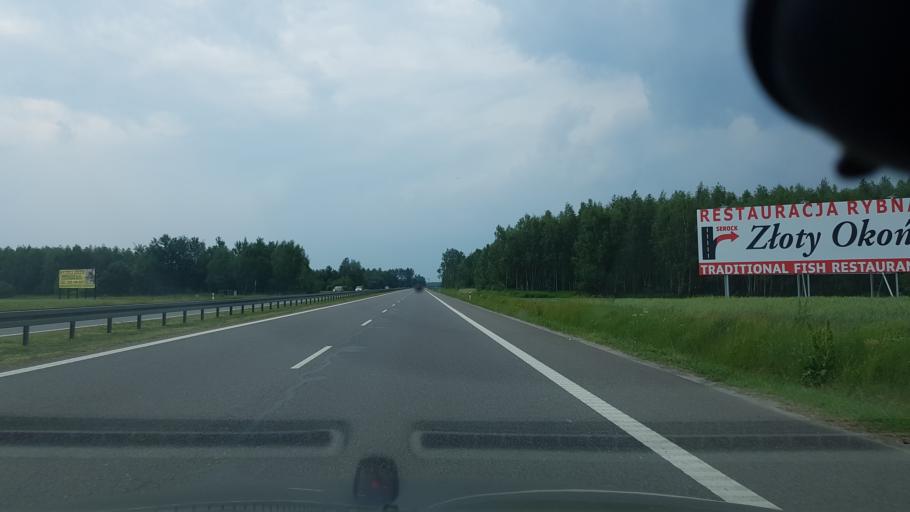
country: PL
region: Masovian Voivodeship
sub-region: Powiat legionowski
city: Serock
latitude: 52.4968
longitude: 21.0481
